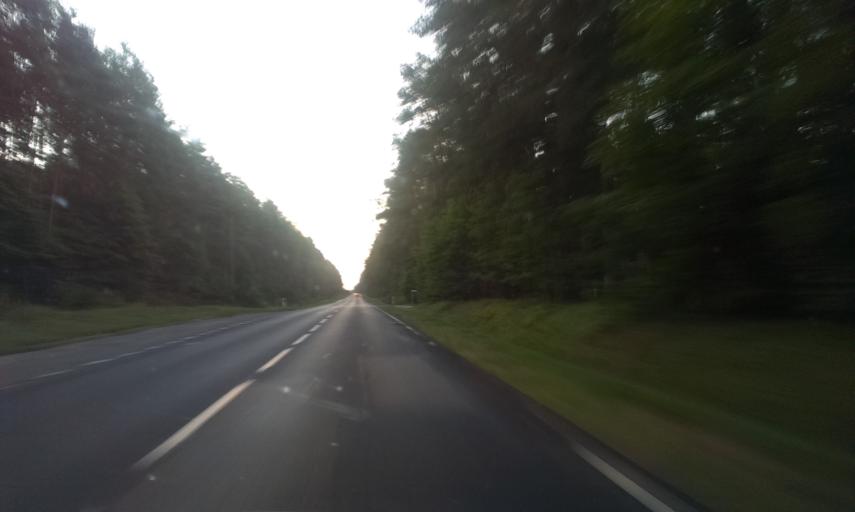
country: PL
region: Kujawsko-Pomorskie
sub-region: Powiat tucholski
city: Tuchola
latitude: 53.5474
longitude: 17.9282
